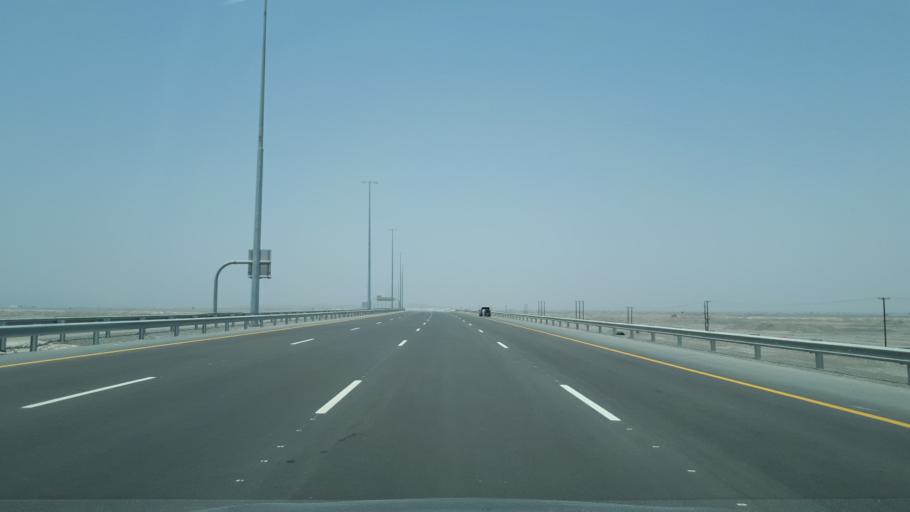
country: OM
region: Al Batinah
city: Barka'
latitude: 23.5706
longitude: 57.7146
